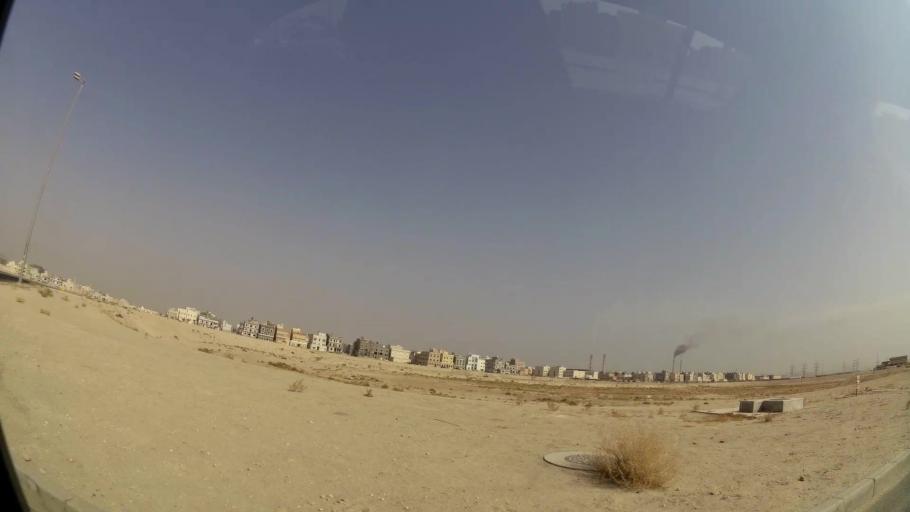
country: KW
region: Muhafazat al Jahra'
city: Al Jahra'
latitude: 29.3417
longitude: 47.7705
